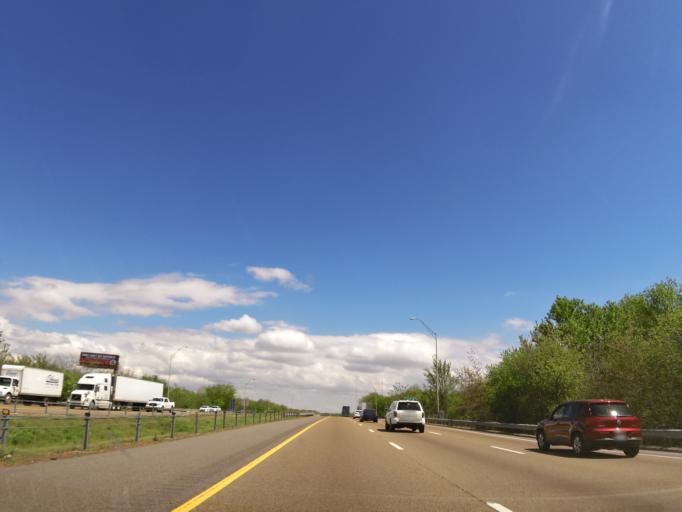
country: US
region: Tennessee
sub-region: Shelby County
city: Memphis
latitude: 35.1910
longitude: -89.9661
